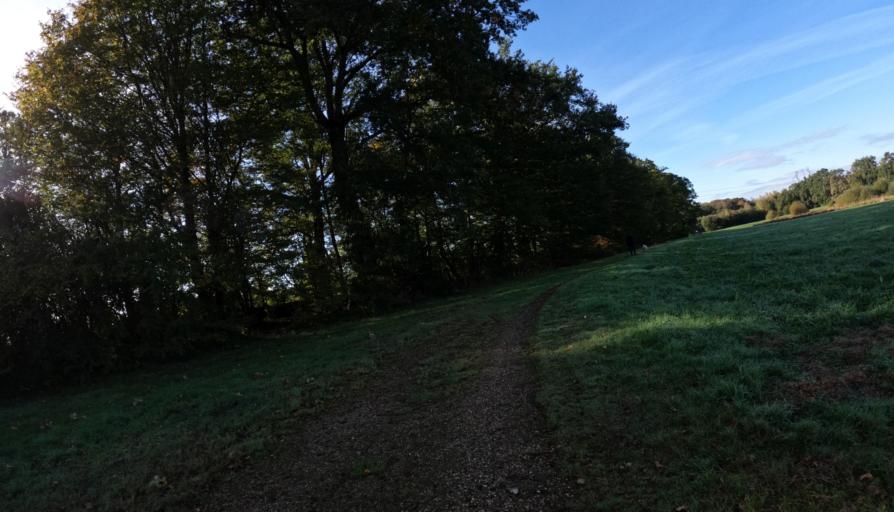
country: FR
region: Brittany
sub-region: Departement d'Ille-et-Vilaine
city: Betton
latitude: 48.1600
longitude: -1.6431
